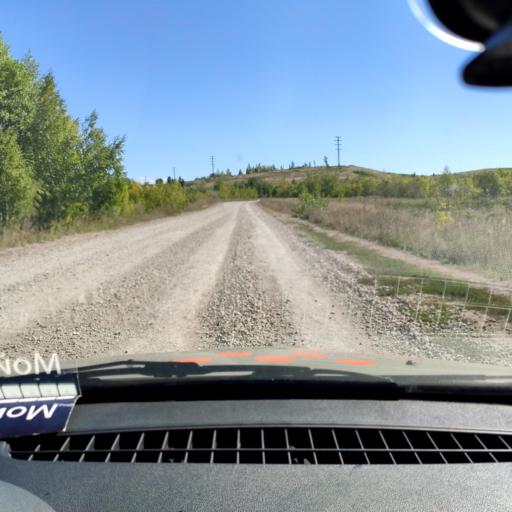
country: RU
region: Bashkortostan
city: Yermolayevo
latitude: 52.7483
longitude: 55.8312
